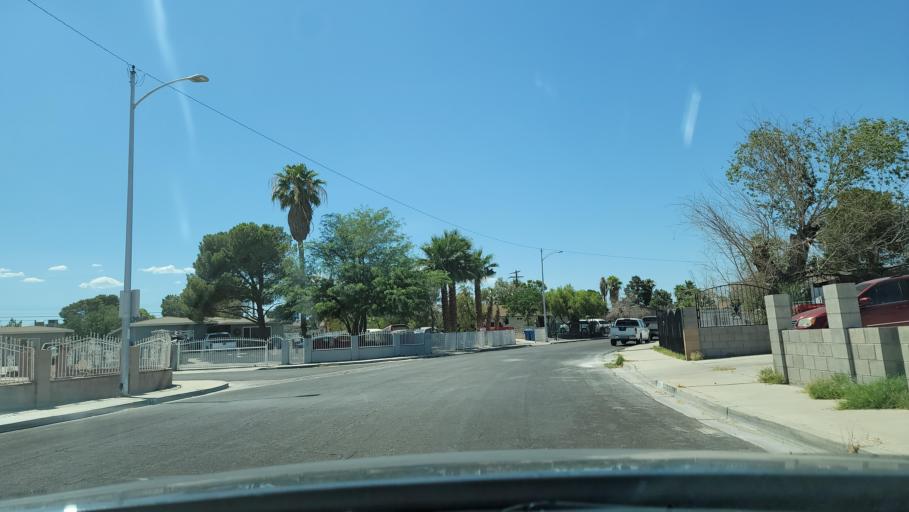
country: US
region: Nevada
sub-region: Clark County
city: Las Vegas
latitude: 36.1788
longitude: -115.1230
